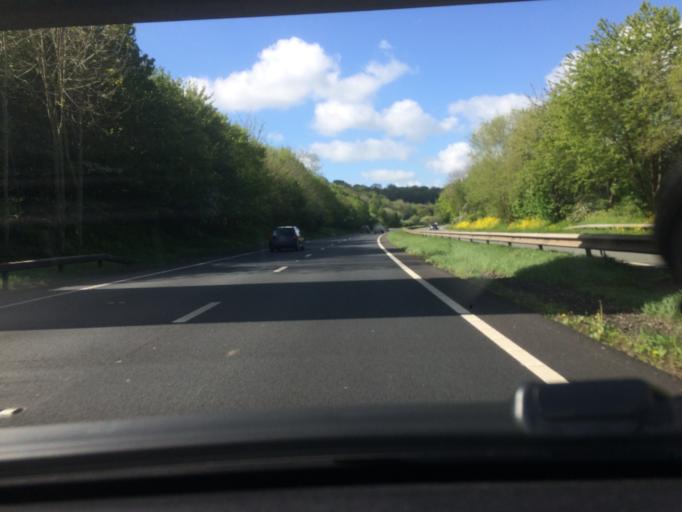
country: GB
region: Wales
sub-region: Wrexham
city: Gresford
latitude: 53.0944
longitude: -2.9686
